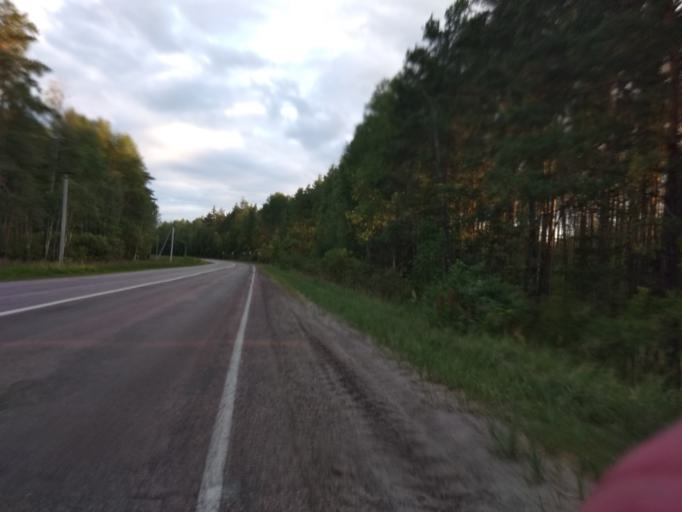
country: RU
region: Moskovskaya
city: Misheronskiy
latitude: 55.6258
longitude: 39.7362
